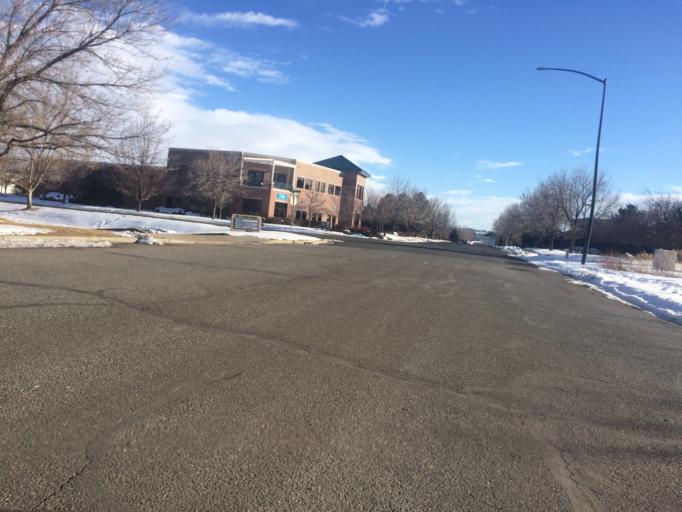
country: US
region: Colorado
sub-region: Boulder County
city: Louisville
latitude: 39.9655
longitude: -105.1249
